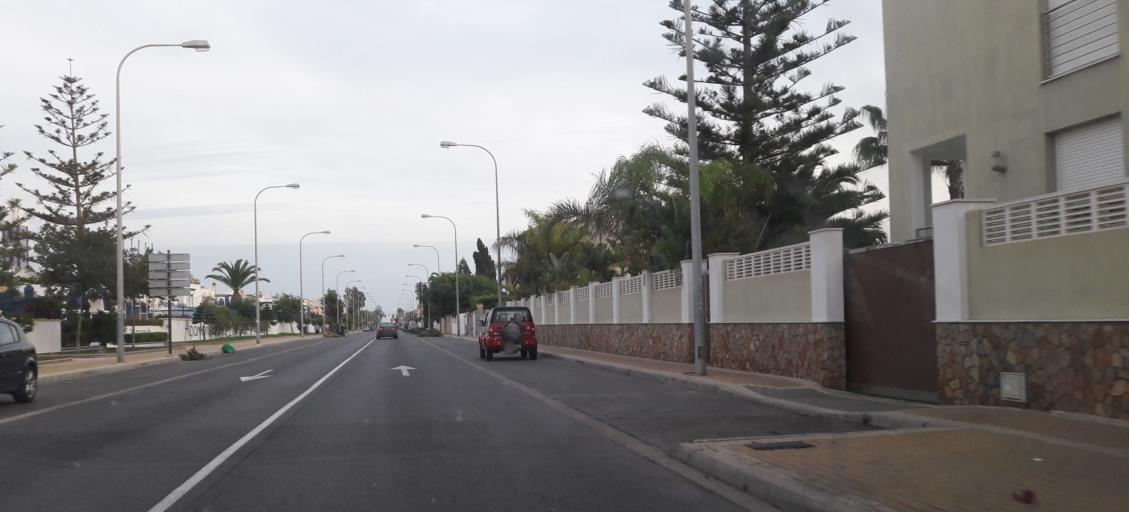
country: ES
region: Andalusia
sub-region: Provincia de Almeria
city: Roquetas de Mar
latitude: 36.7312
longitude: -2.6291
